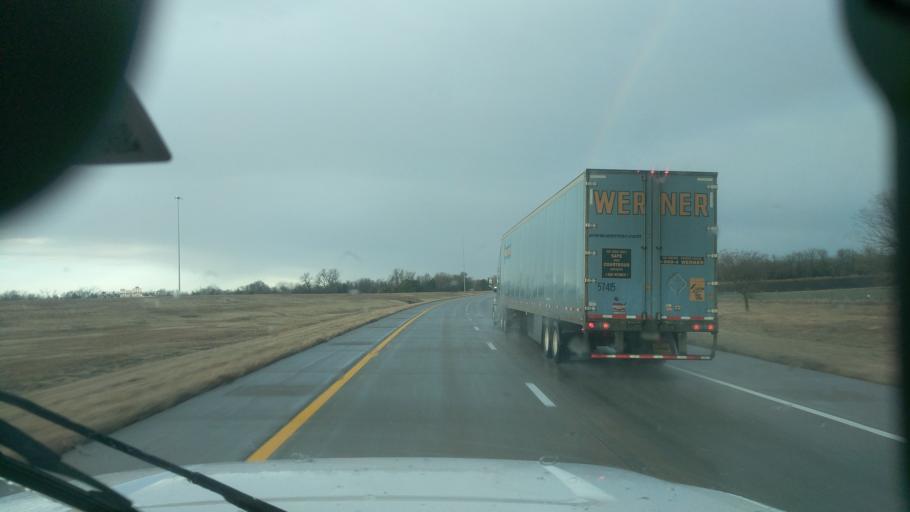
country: US
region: Kansas
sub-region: Harvey County
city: Newton
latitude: 38.0271
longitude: -97.3278
